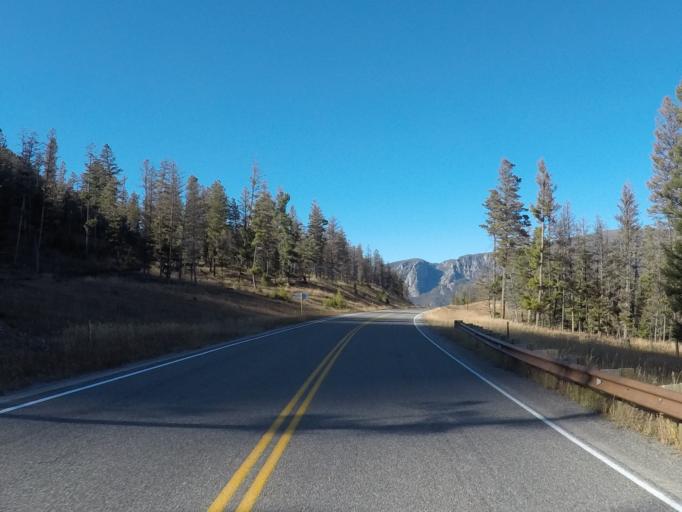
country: US
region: Montana
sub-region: Carbon County
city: Red Lodge
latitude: 44.8237
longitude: -109.4692
